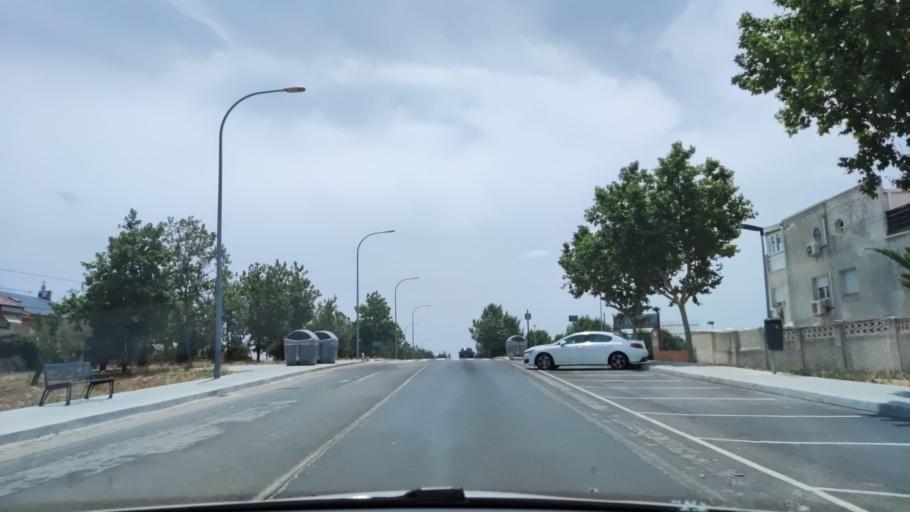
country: ES
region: Madrid
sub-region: Provincia de Madrid
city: Navalcarnero
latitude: 40.2841
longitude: -4.0225
